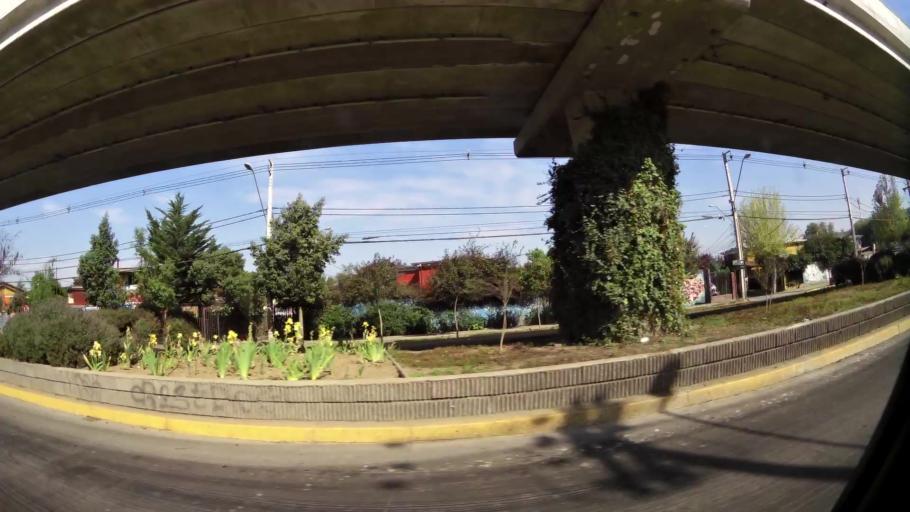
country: CL
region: Santiago Metropolitan
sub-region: Provincia de Santiago
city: Lo Prado
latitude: -33.4587
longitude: -70.7382
